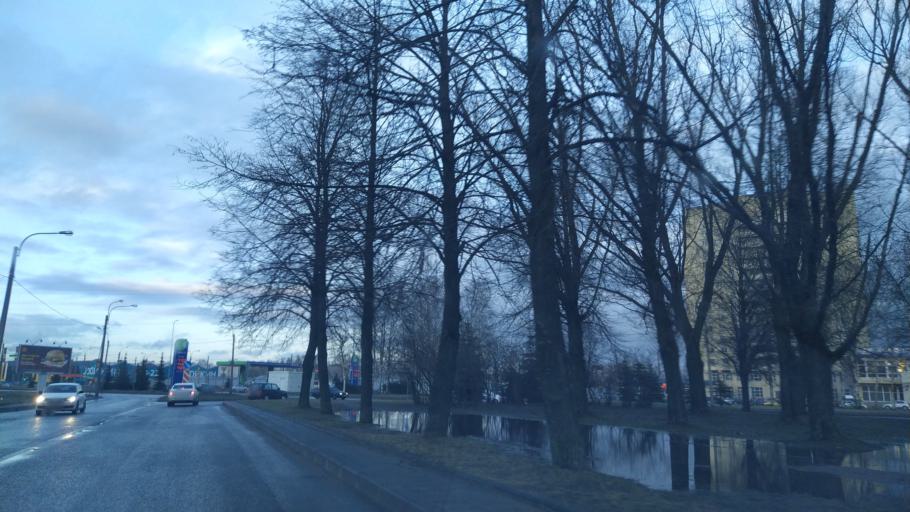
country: RU
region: St.-Petersburg
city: Grazhdanka
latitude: 60.0138
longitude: 30.4315
